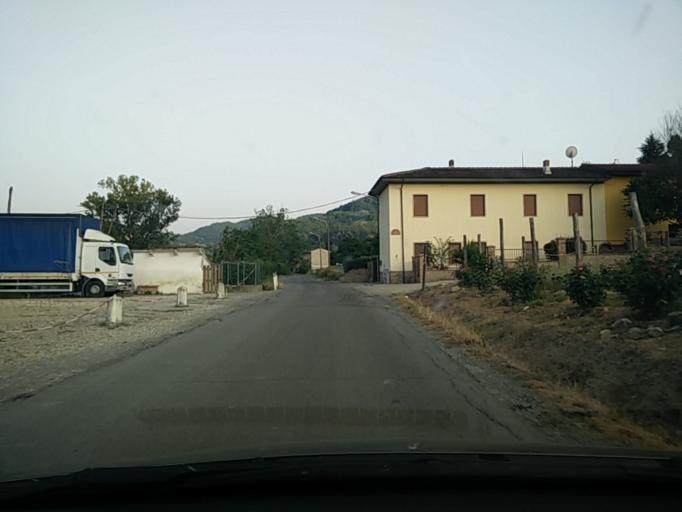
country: IT
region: Lombardy
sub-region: Provincia di Pavia
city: Montesegale
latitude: 44.9375
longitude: 9.1170
